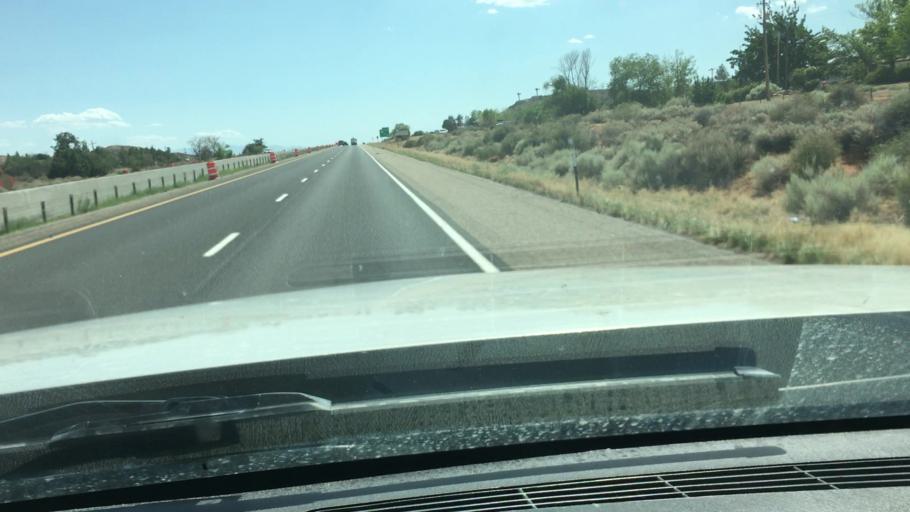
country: US
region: Utah
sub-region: Washington County
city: Toquerville
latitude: 37.2493
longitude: -113.3454
